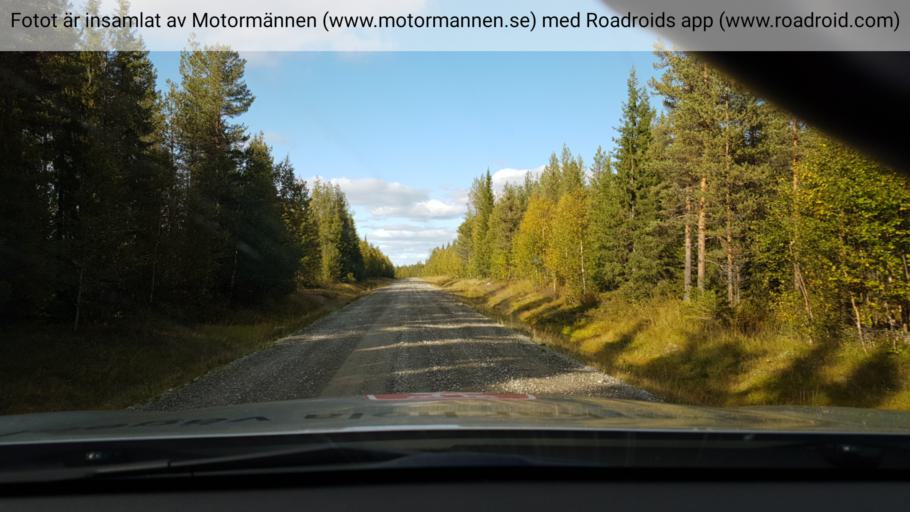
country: SE
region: Vaesterbotten
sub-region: Sorsele Kommun
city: Sorsele
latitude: 65.4170
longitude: 18.1066
